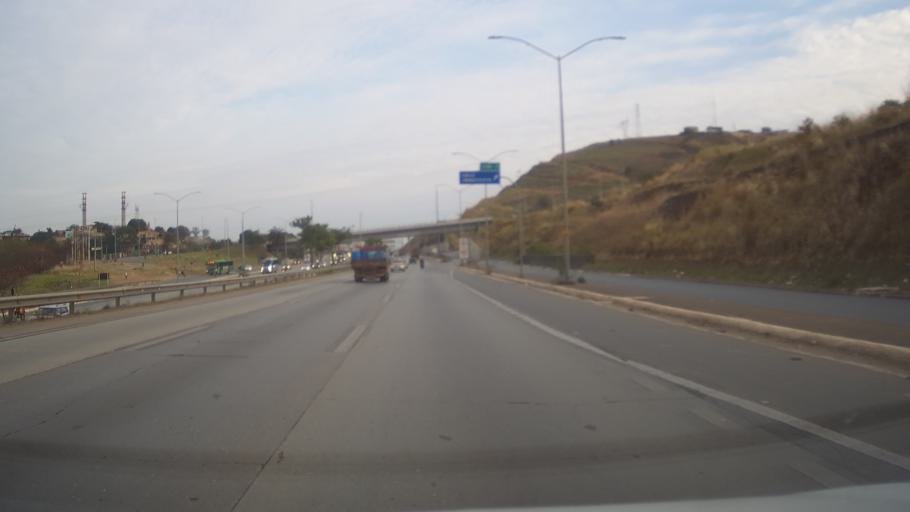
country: BR
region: Minas Gerais
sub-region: Vespasiano
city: Vespasiano
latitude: -19.7821
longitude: -43.9486
